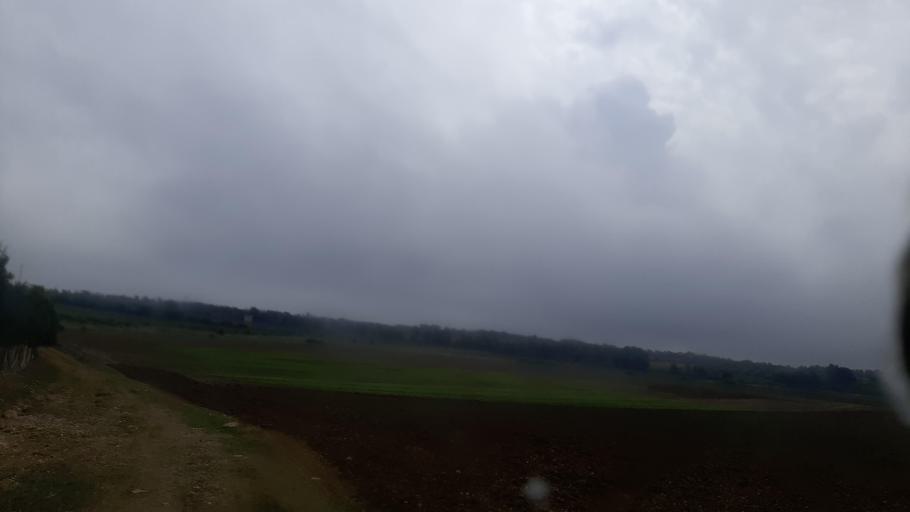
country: TN
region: Nabul
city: Qulaybiyah
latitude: 36.8270
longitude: 11.0357
